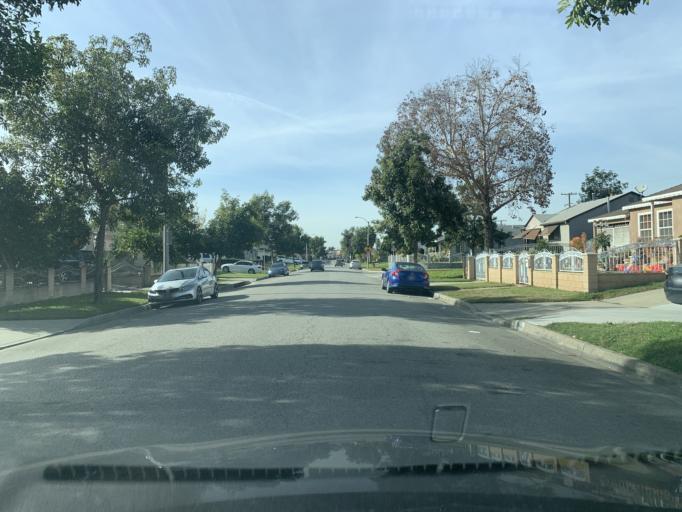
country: US
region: California
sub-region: Los Angeles County
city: Rosemead
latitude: 34.0732
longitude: -118.0605
